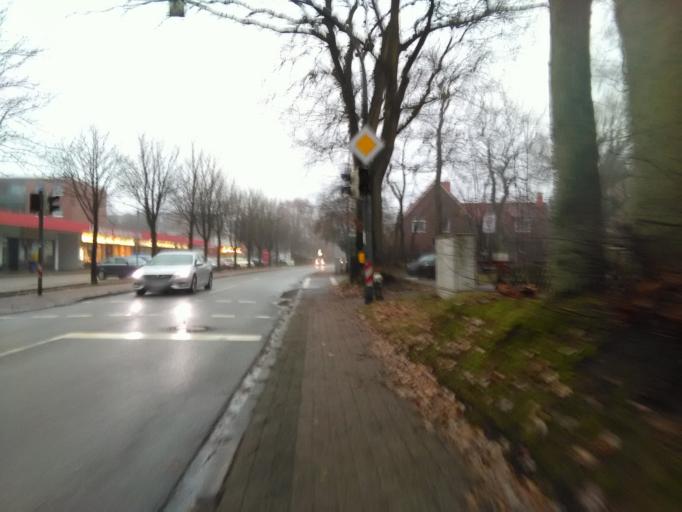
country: DE
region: Schleswig-Holstein
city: Quickborn
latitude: 53.7273
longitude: 9.9135
